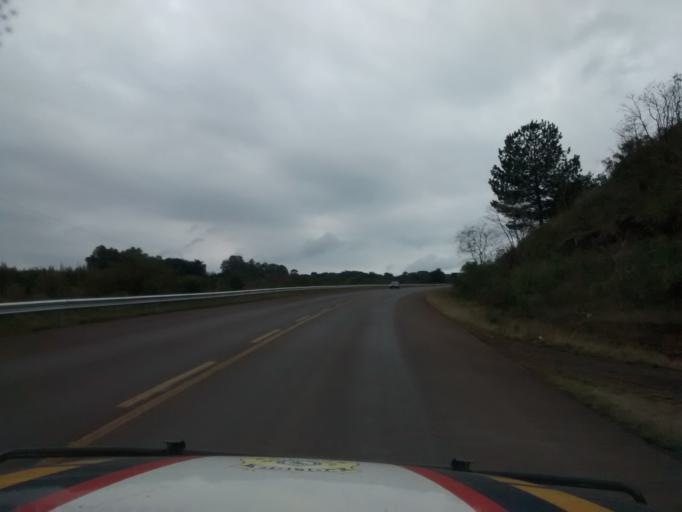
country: BR
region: Rio Grande do Sul
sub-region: Lagoa Vermelha
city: Lagoa Vermelha
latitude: -28.2289
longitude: -51.6244
